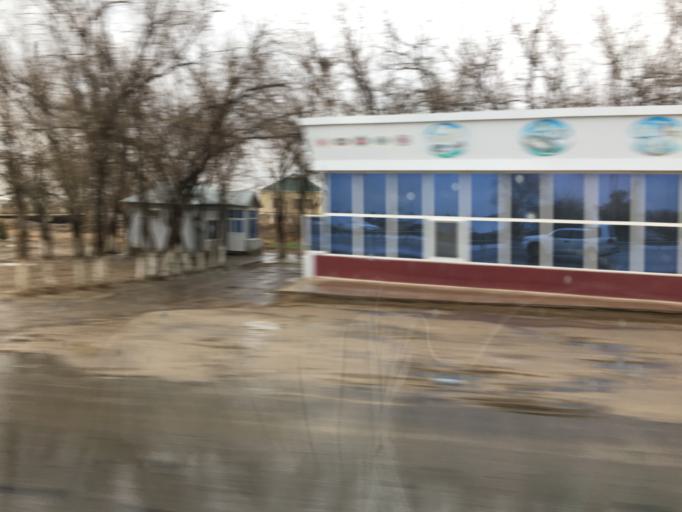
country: TM
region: Mary
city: Mary
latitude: 37.5369
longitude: 61.8833
